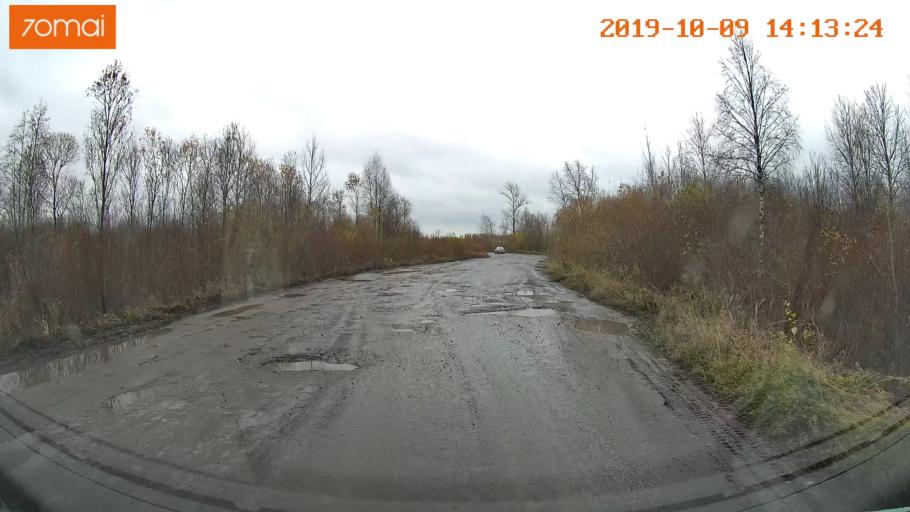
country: RU
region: Kostroma
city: Buy
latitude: 58.4813
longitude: 41.5115
